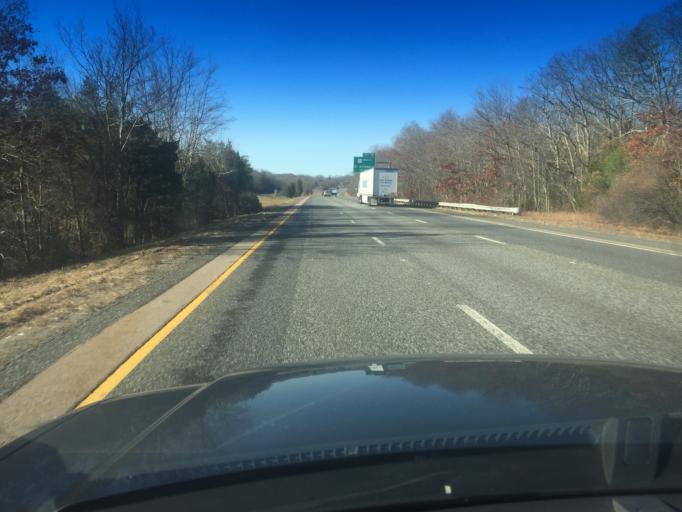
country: US
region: Massachusetts
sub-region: Bristol County
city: Attleboro
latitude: 41.9511
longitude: -71.3327
